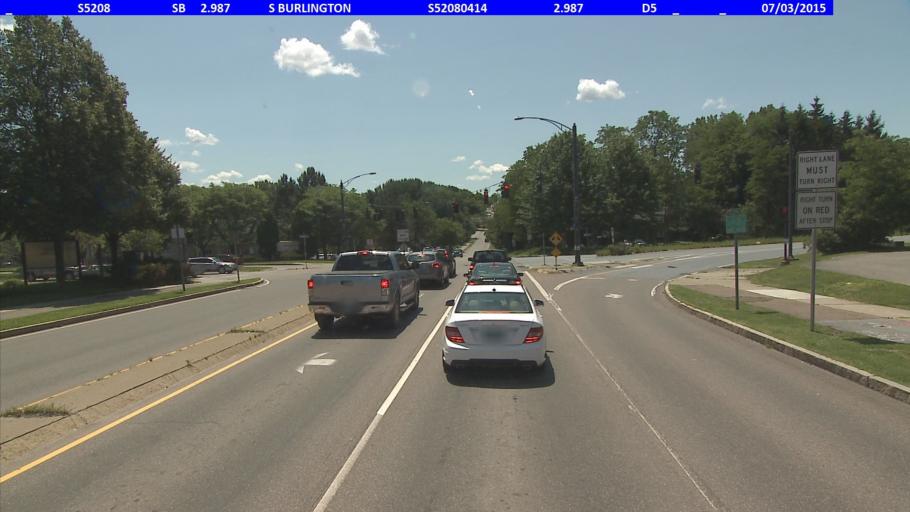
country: US
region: Vermont
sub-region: Chittenden County
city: South Burlington
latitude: 44.4533
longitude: -73.1788
